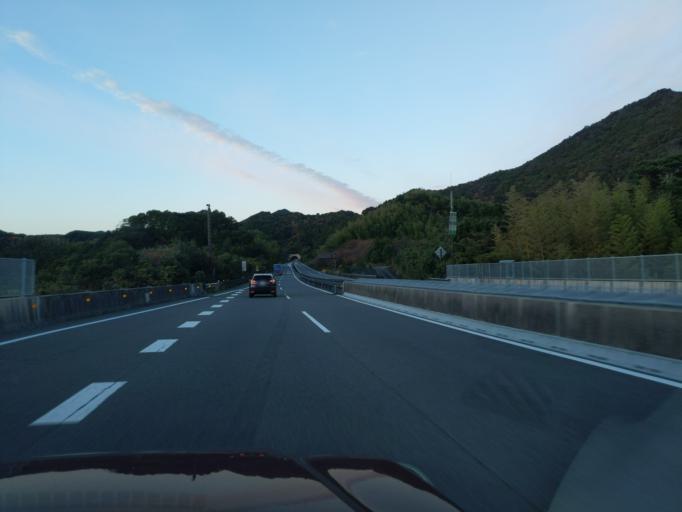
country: JP
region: Tokushima
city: Anan
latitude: 33.7747
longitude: 134.5820
